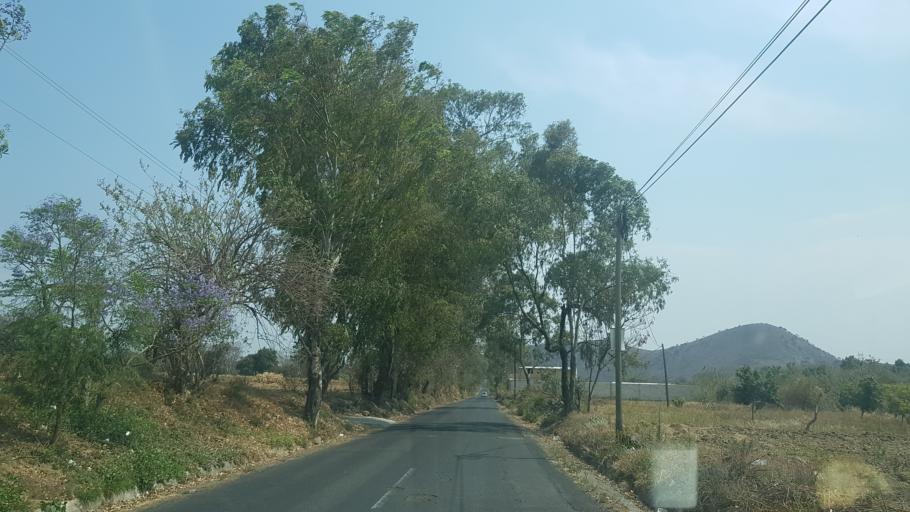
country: MX
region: Puebla
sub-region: Tianguismanalco
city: San Martin Tlapala
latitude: 18.9593
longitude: -98.4590
